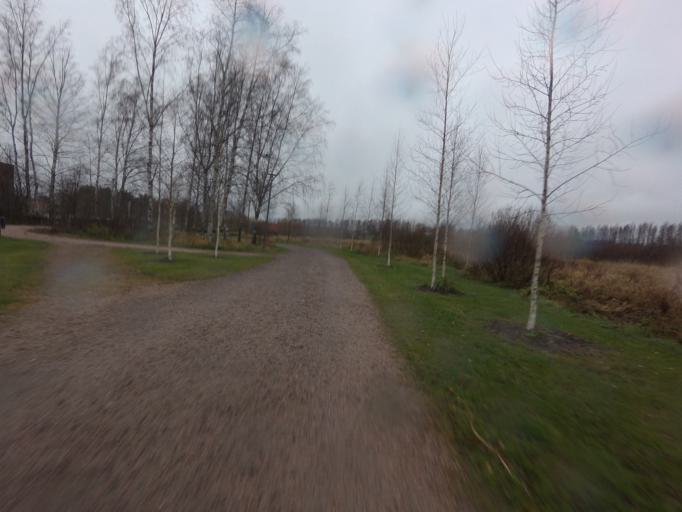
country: FI
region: Uusimaa
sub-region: Helsinki
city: Espoo
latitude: 60.2104
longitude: 24.6657
